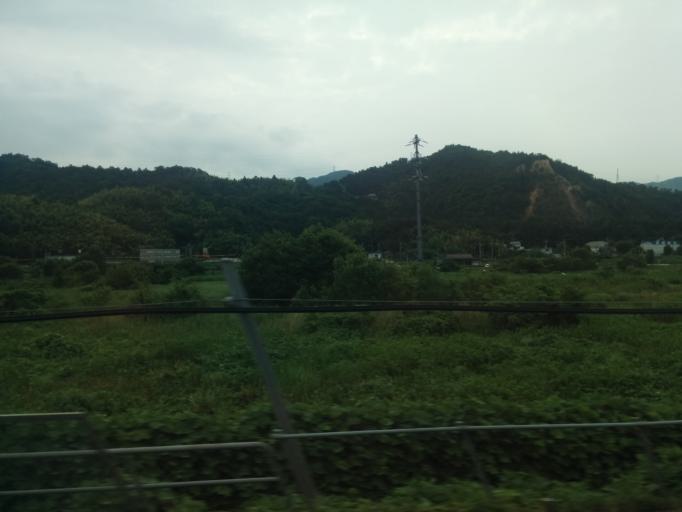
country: JP
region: Shiga Prefecture
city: Hikone
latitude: 35.2948
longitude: 136.2825
